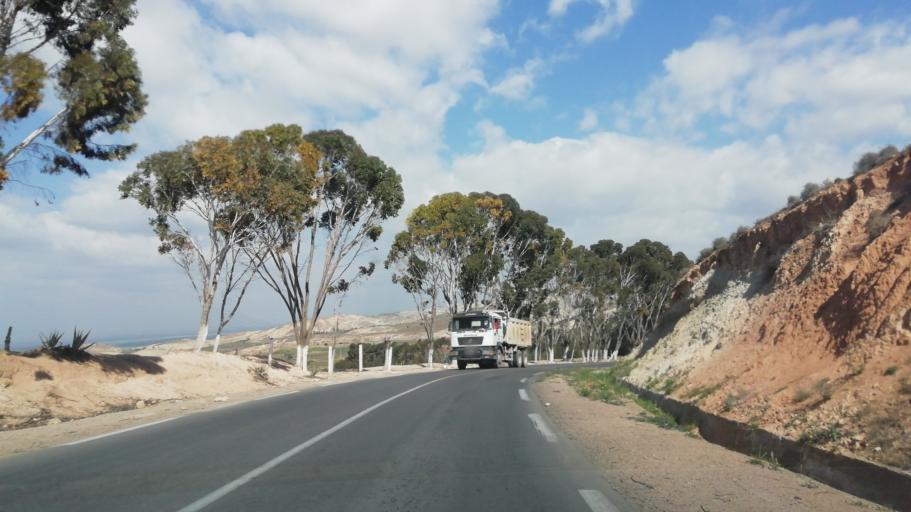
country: DZ
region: Mascara
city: Mascara
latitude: 35.5463
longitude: 0.0827
